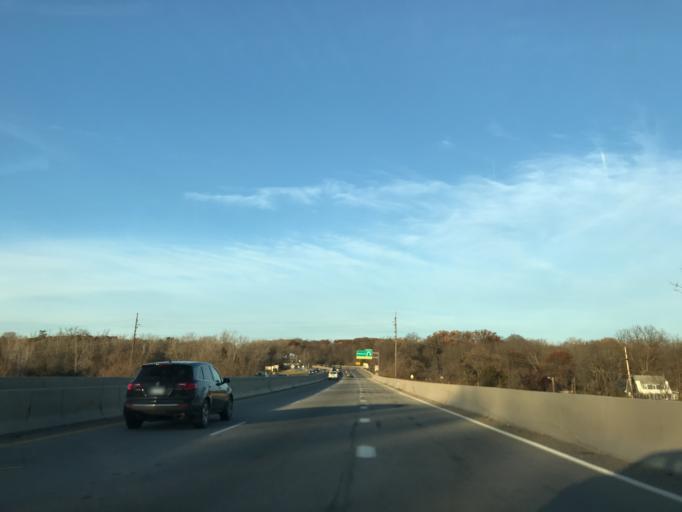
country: US
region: Michigan
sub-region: Washtenaw County
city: Ann Arbor
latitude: 42.3021
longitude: -83.7458
